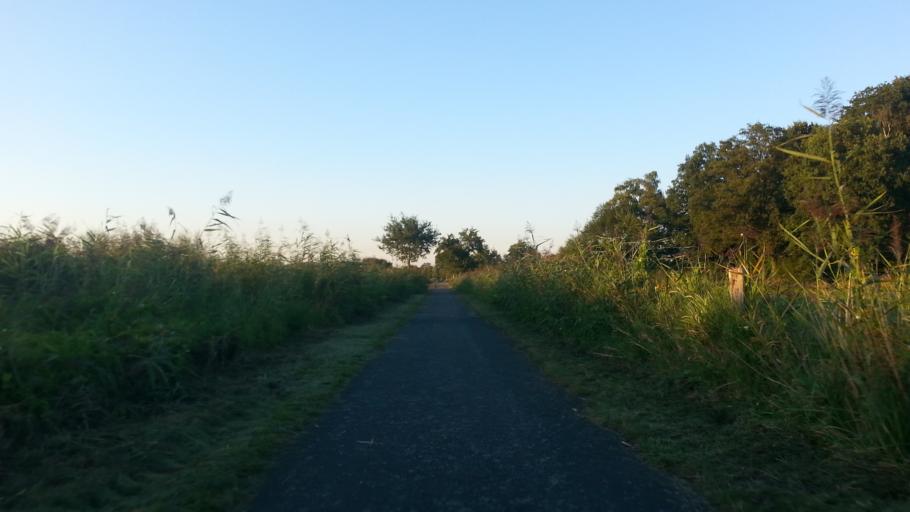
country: DE
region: North Rhine-Westphalia
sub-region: Regierungsbezirk Munster
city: Muenster
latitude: 52.0195
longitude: 7.6587
